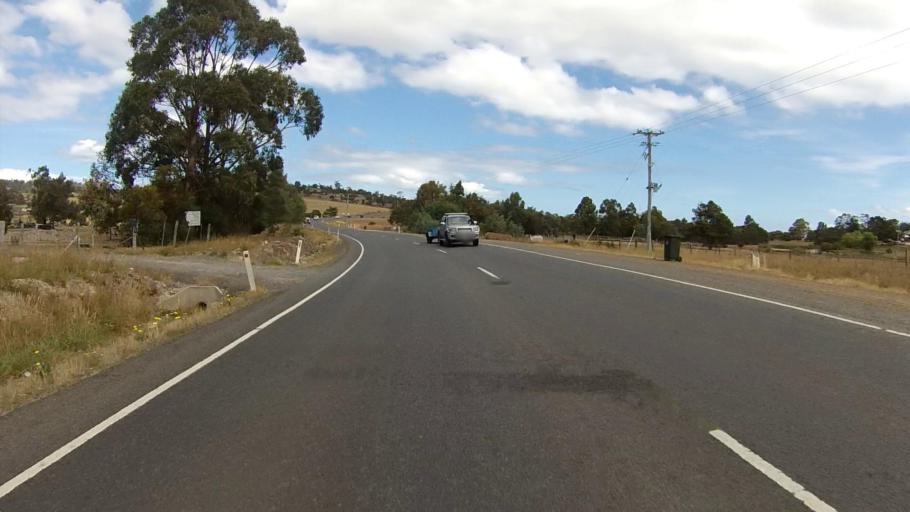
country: AU
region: Tasmania
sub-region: Sorell
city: Sorell
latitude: -42.8303
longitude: 147.6235
